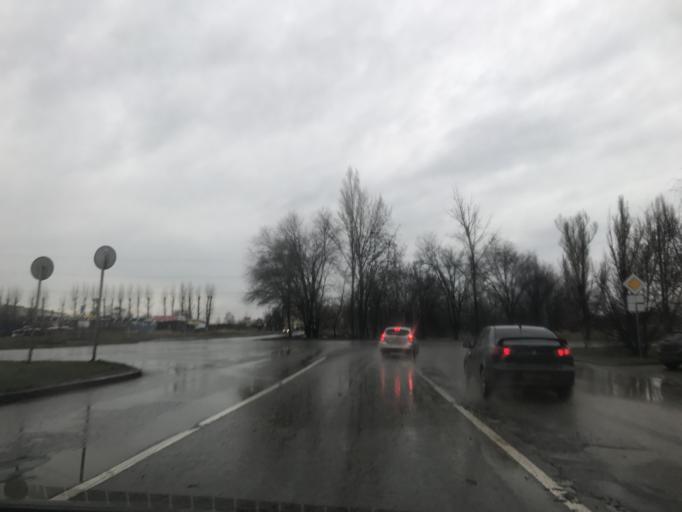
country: RU
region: Rostov
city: Severnyy
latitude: 47.2997
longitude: 39.7123
